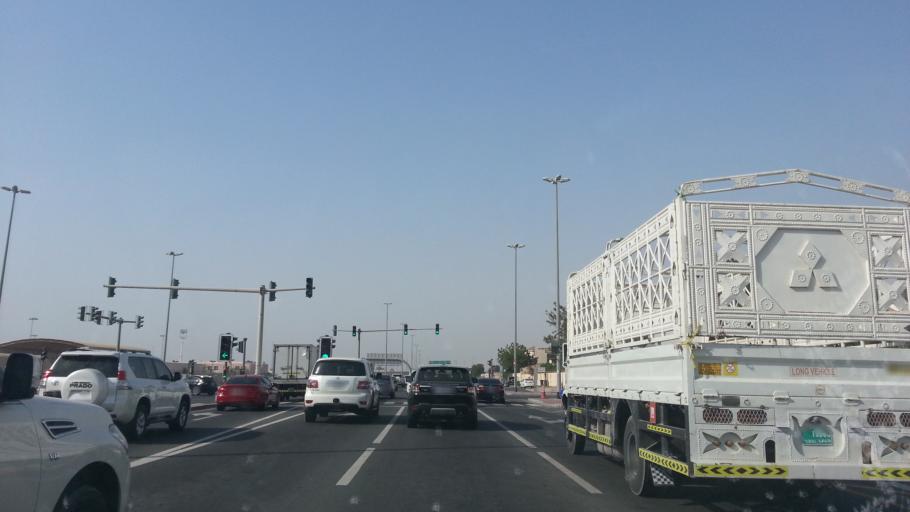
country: AE
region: Dubai
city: Dubai
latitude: 25.1119
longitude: 55.2078
